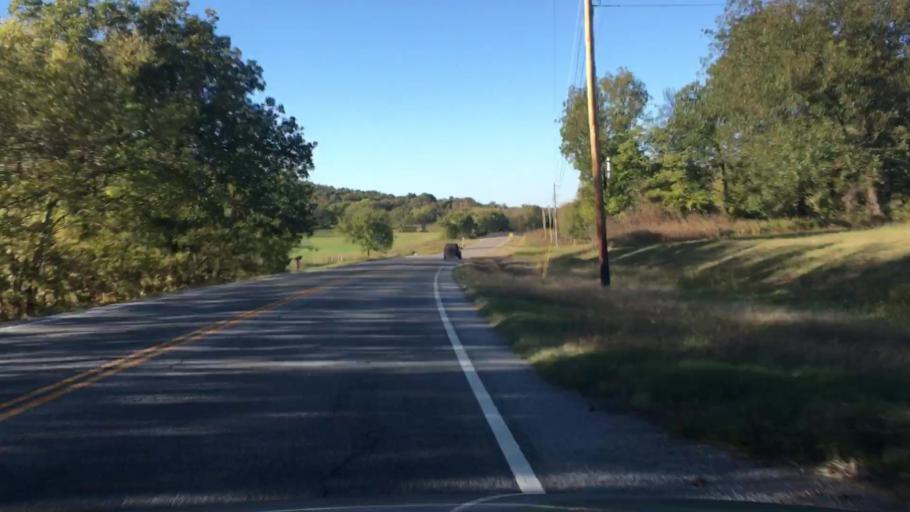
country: US
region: Oklahoma
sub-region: Cherokee County
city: Tahlequah
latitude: 35.9180
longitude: -95.1220
